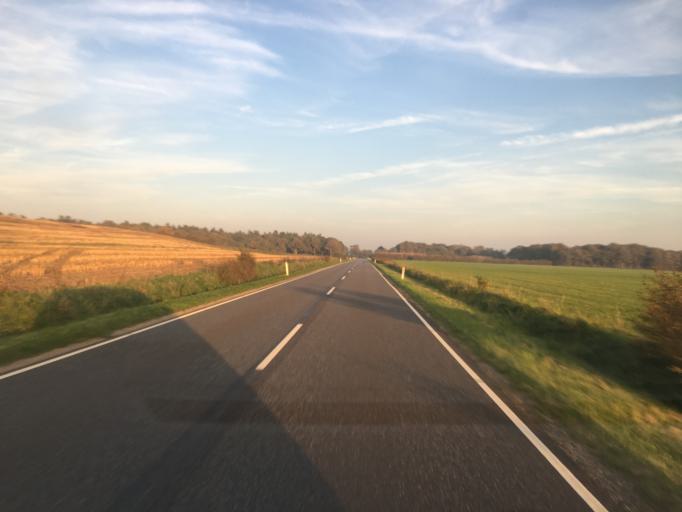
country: DK
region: South Denmark
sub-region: Tonder Kommune
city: Logumkloster
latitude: 55.0477
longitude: 9.0621
